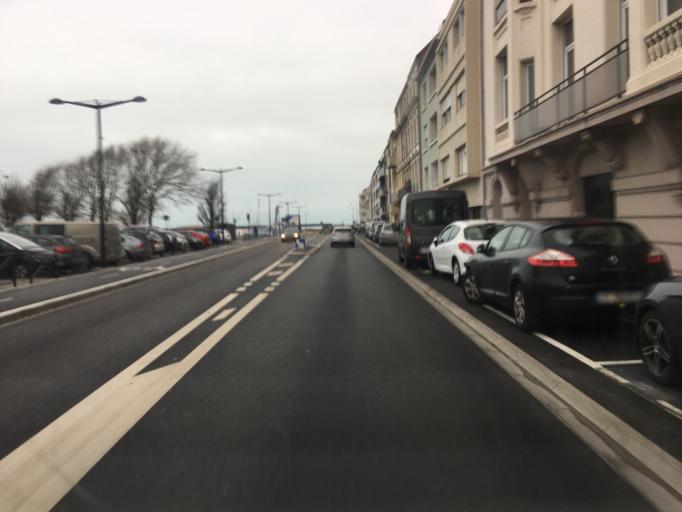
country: FR
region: Nord-Pas-de-Calais
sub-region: Departement du Pas-de-Calais
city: Saint-Martin-Boulogne
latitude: 50.7333
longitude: 1.5949
